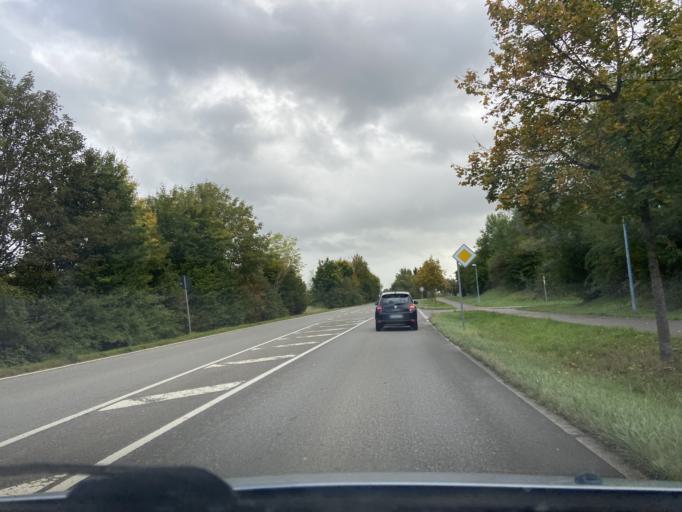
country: DE
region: Baden-Wuerttemberg
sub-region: Tuebingen Region
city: Sigmaringen
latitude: 48.0965
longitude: 9.2394
